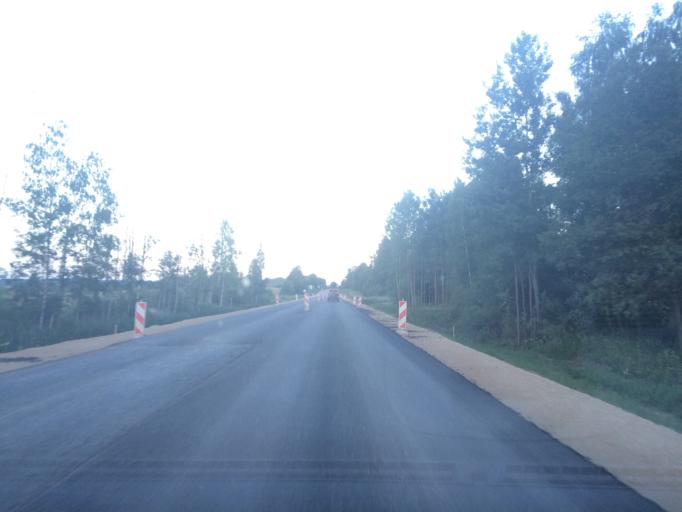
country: LT
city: Zarasai
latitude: 55.7499
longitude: 26.3177
